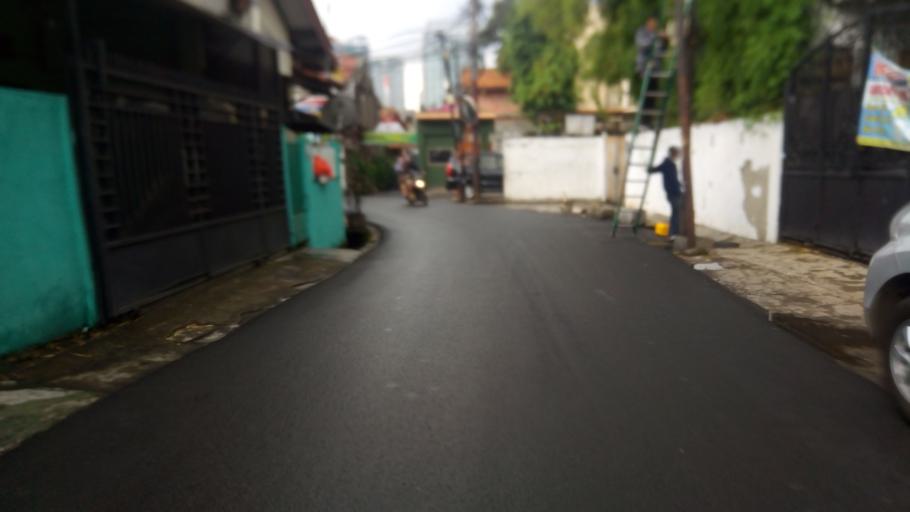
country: ID
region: Jakarta Raya
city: Jakarta
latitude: -6.2623
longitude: 106.8053
